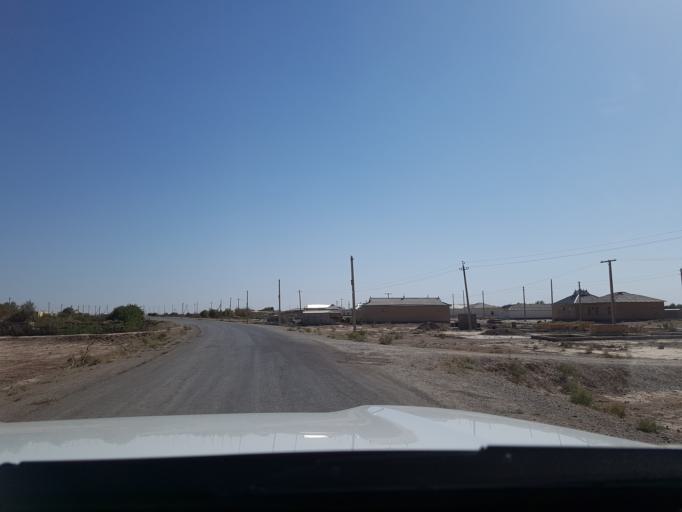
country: IR
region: Razavi Khorasan
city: Sarakhs
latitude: 36.5193
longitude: 61.2507
